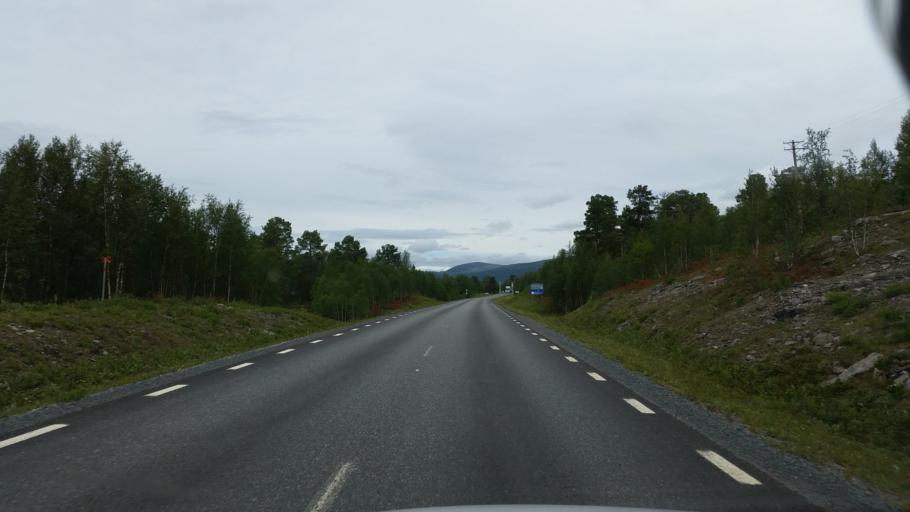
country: NO
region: Nordland
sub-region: Sorfold
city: Straumen
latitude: 66.5426
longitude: 16.3330
